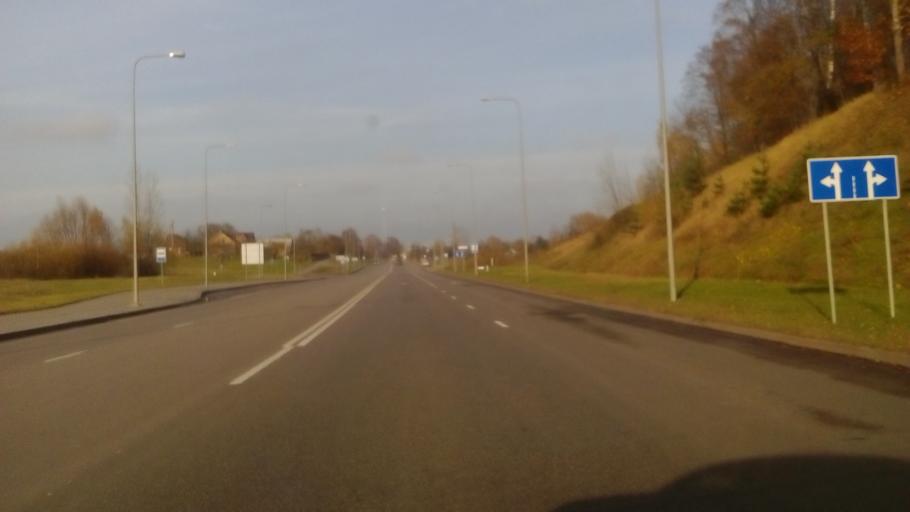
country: LT
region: Alytaus apskritis
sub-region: Alytus
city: Alytus
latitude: 54.4036
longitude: 24.0023
